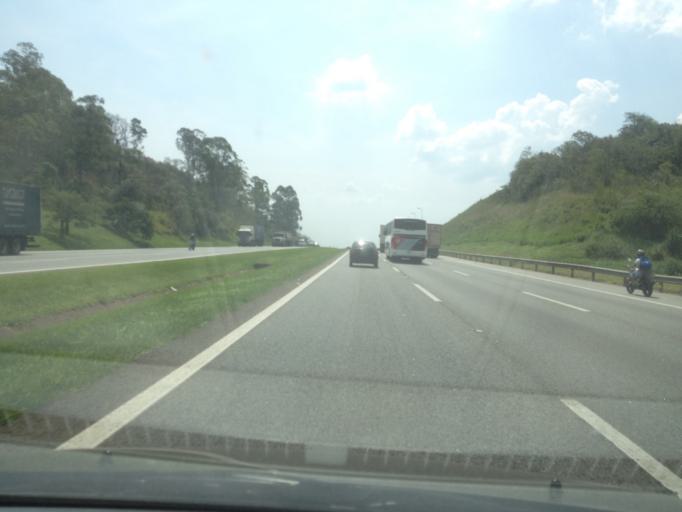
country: BR
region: Sao Paulo
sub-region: Pirapora Do Bom Jesus
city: Pirapora do Bom Jesus
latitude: -23.4665
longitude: -47.0253
